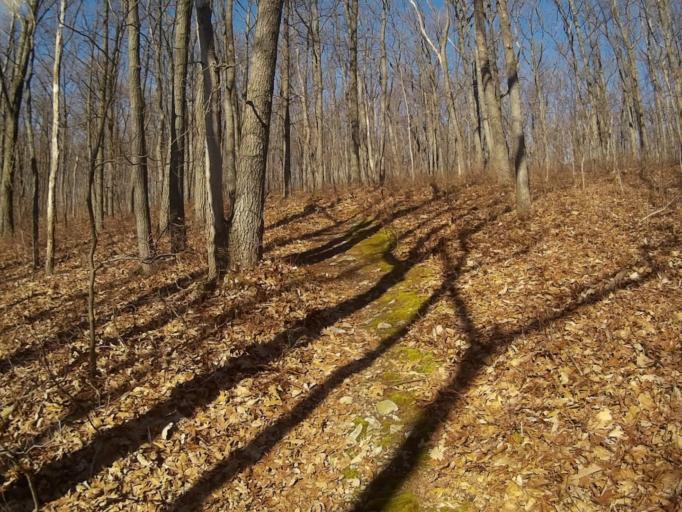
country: US
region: Pennsylvania
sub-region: Centre County
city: Lemont
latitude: 40.8075
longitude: -77.7985
